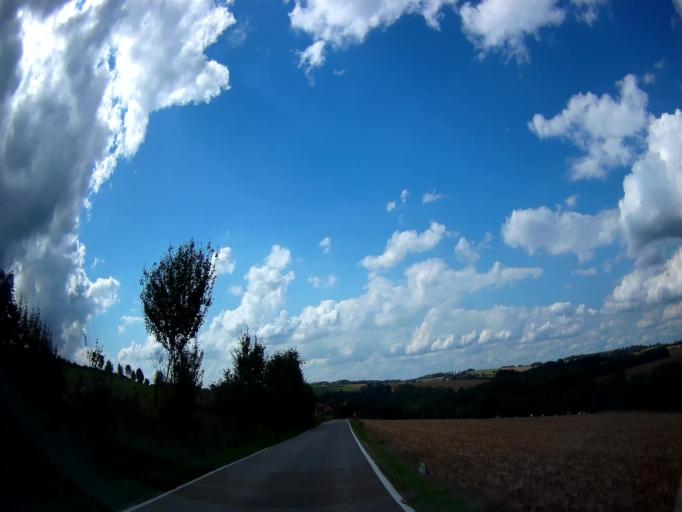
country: BE
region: Wallonia
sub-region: Province de Namur
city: Assesse
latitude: 50.3542
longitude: 4.9756
